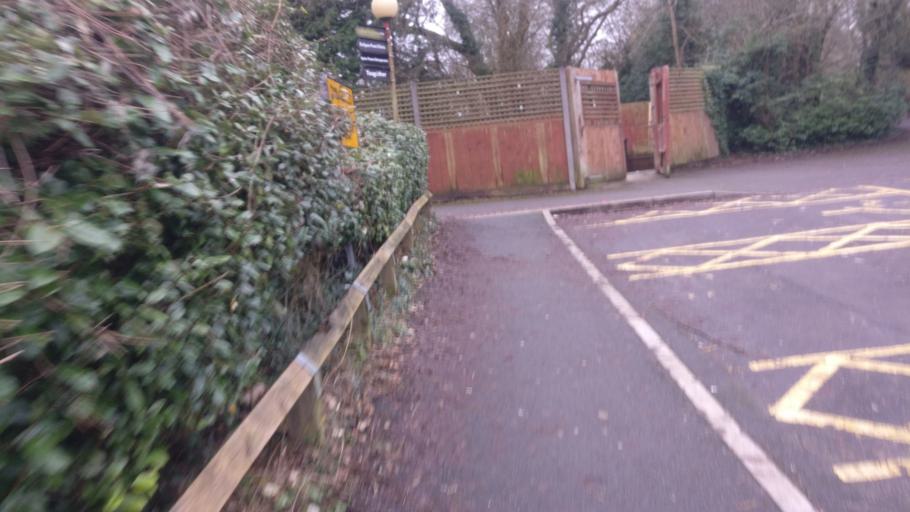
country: GB
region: England
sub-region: Hampshire
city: Old Basing
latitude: 51.2766
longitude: -1.0580
